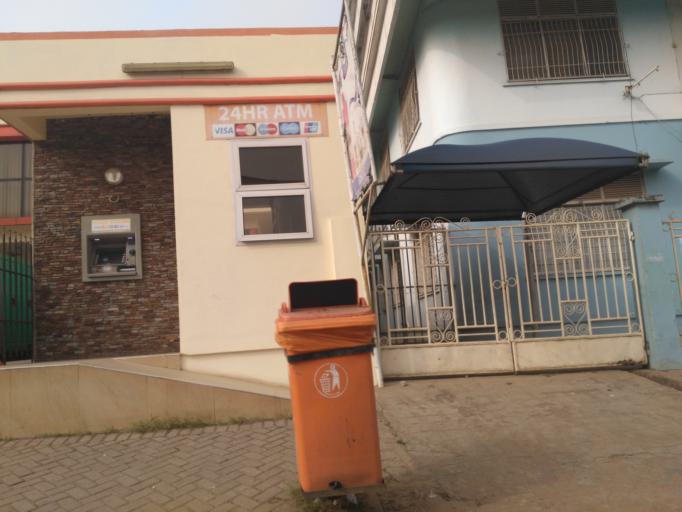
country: GH
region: Ashanti
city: Kumasi
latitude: 6.6950
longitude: -1.6241
